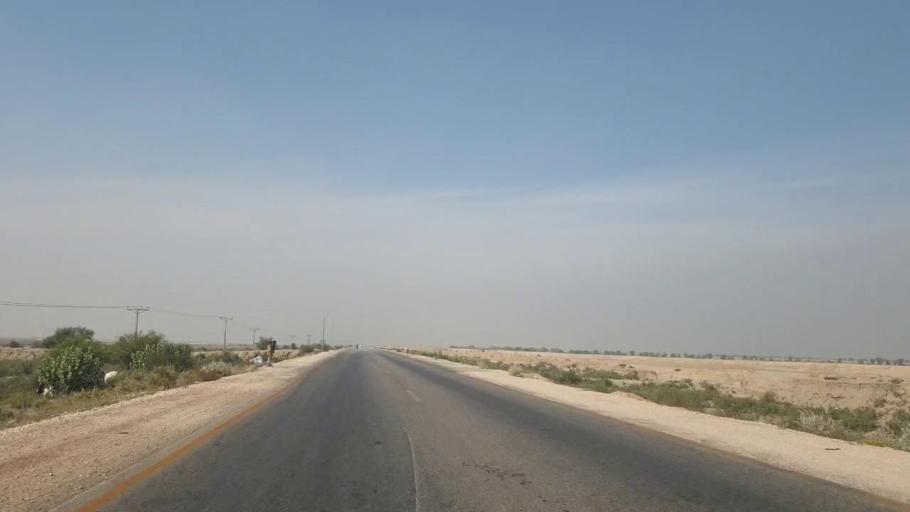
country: PK
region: Sindh
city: Sann
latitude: 25.9099
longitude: 68.2256
